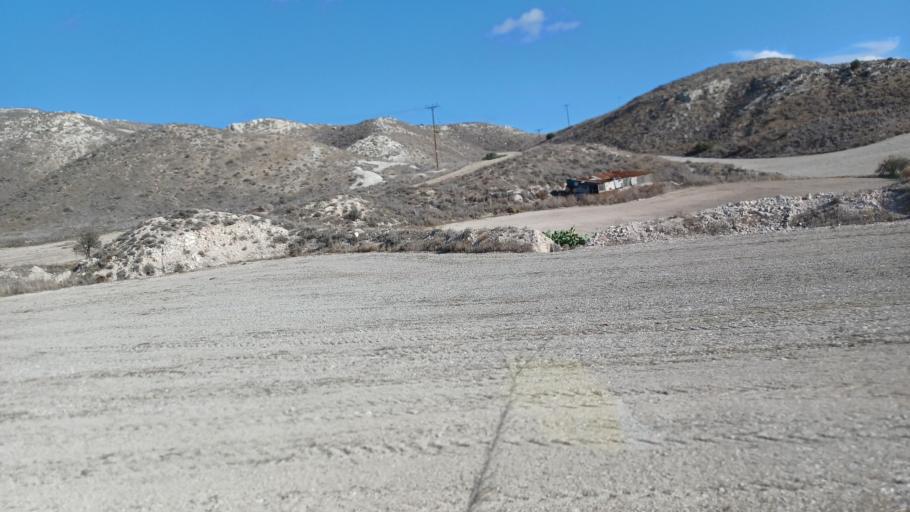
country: CY
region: Larnaka
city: Troulloi
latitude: 35.0286
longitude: 33.5803
